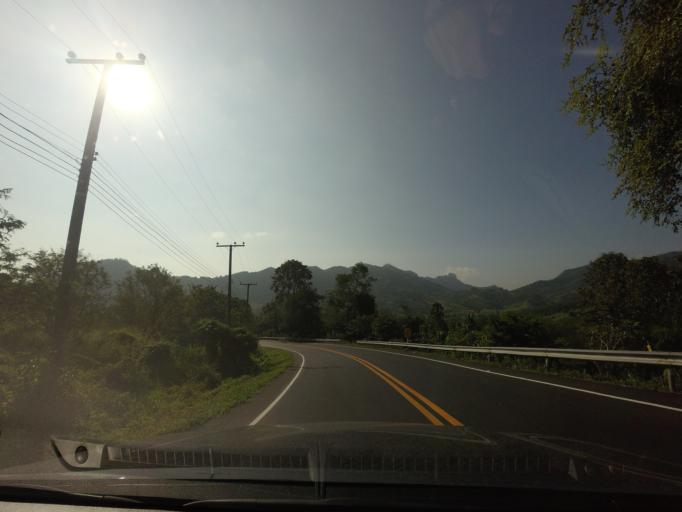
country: TH
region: Phetchabun
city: Lom Kao
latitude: 16.8707
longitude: 101.1329
